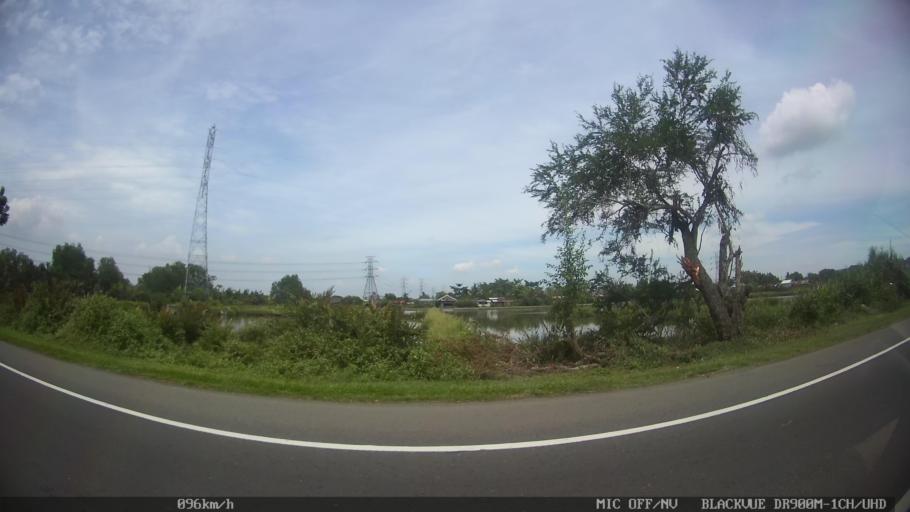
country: ID
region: North Sumatra
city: Belawan
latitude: 3.7520
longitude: 98.6799
